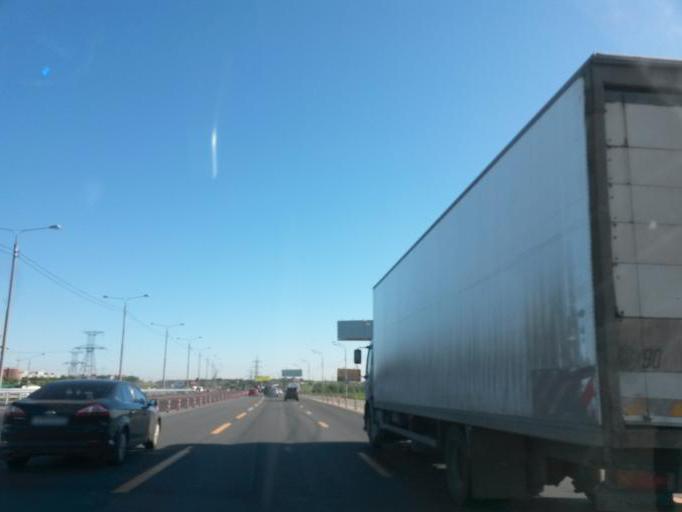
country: RU
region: Moskovskaya
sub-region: Podol'skiy Rayon
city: Podol'sk
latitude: 55.4577
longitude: 37.6196
